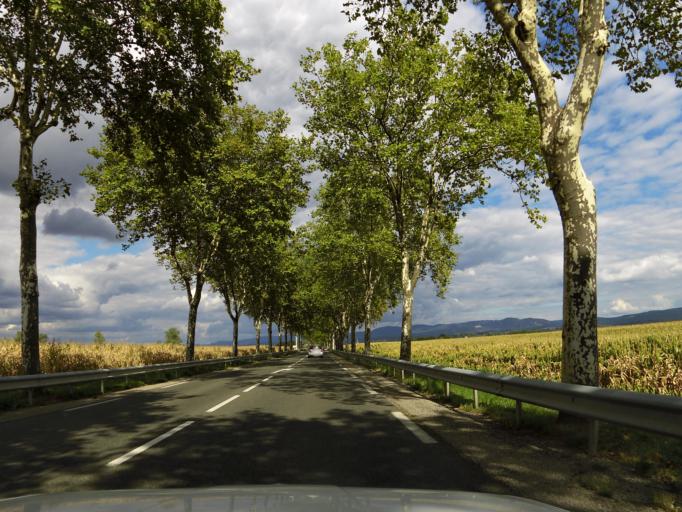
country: FR
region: Rhone-Alpes
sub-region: Departement de l'Ain
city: Chazey-sur-Ain
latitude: 45.9164
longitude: 5.2593
